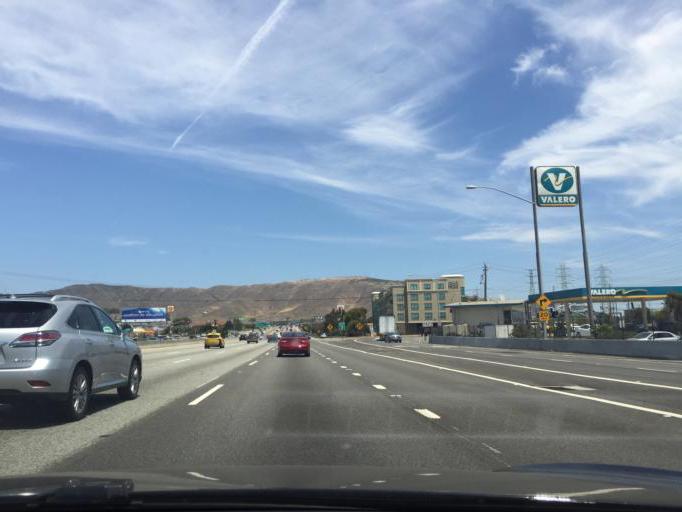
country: US
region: California
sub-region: San Mateo County
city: South San Francisco
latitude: 37.6454
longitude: -122.4062
